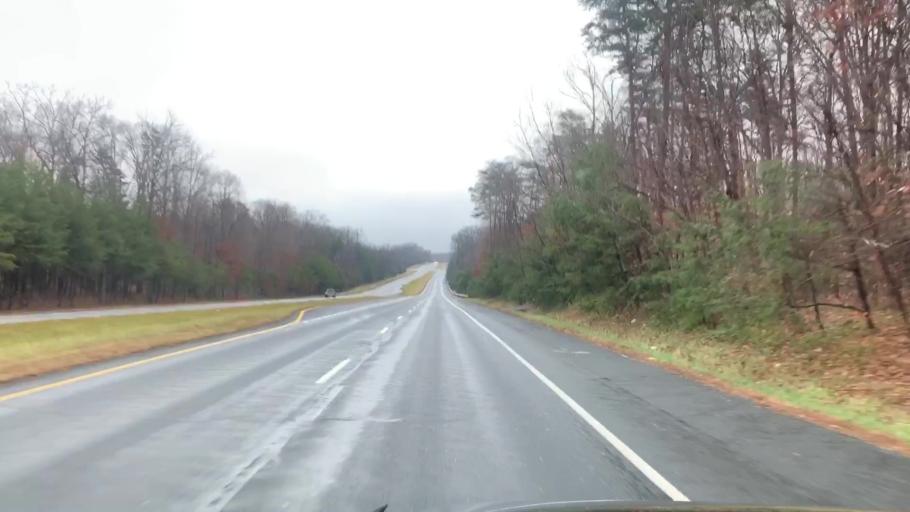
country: US
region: Virginia
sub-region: Fairfax County
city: Fairfax Station
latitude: 38.7746
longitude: -77.3232
